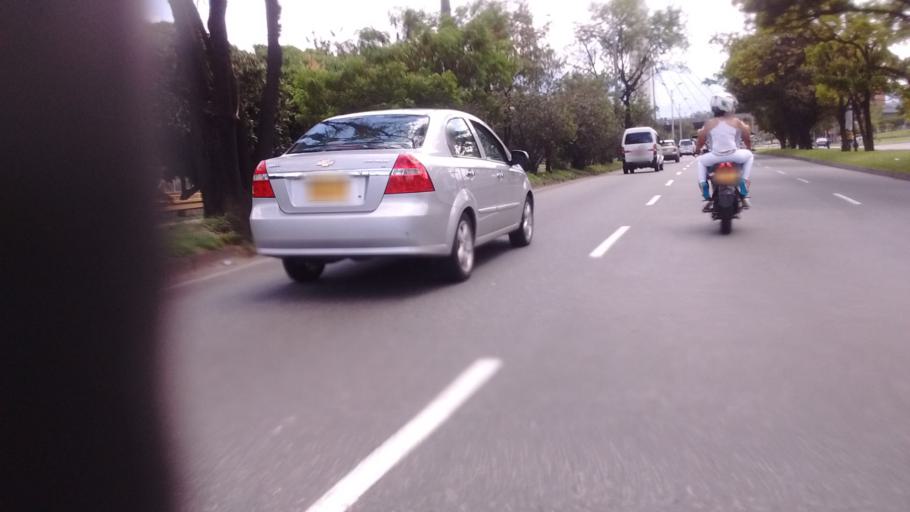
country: CO
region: Antioquia
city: Itagui
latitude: 6.2063
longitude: -75.5795
